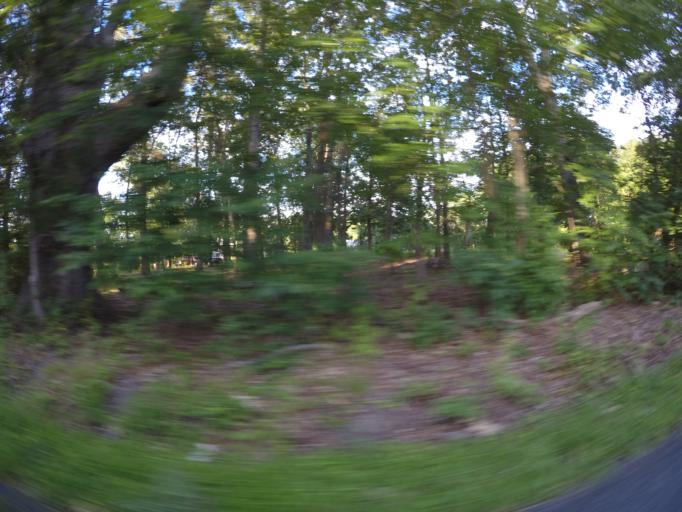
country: US
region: Maryland
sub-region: Harford County
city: Joppatowne
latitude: 39.4686
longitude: -76.3461
